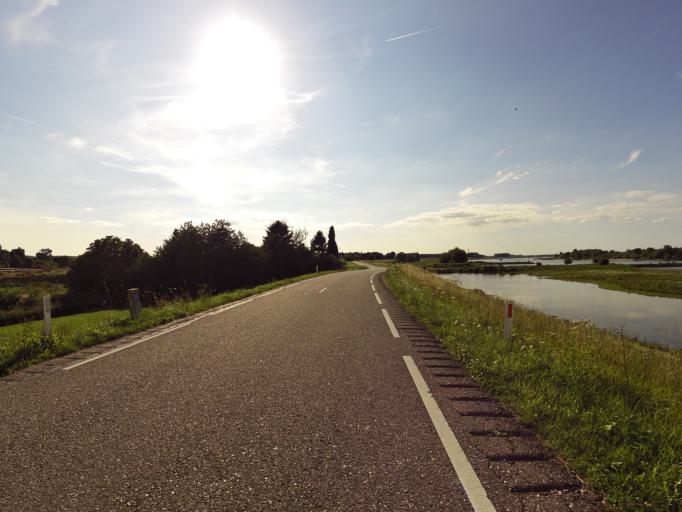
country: NL
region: Gelderland
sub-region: Gemeente Groesbeek
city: Berg en Dal
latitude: 51.8499
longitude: 5.9703
